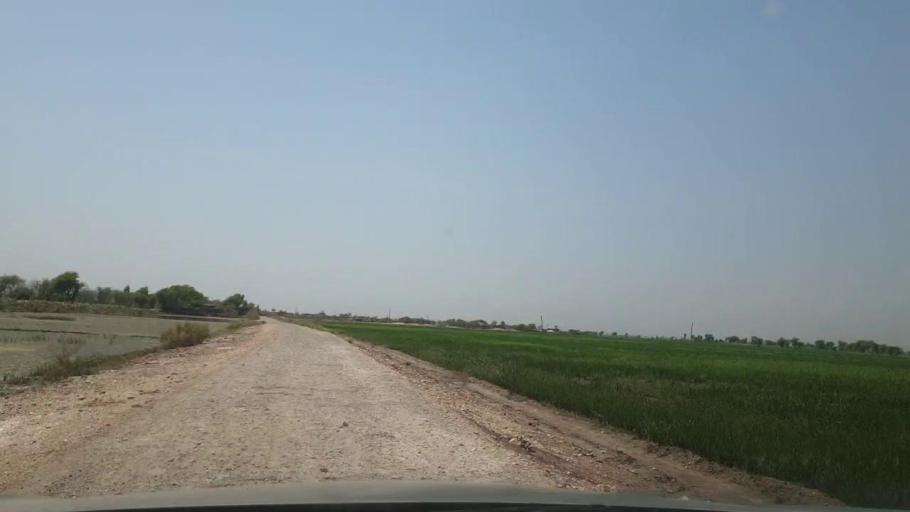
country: PK
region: Sindh
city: Warah
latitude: 27.4863
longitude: 67.7357
